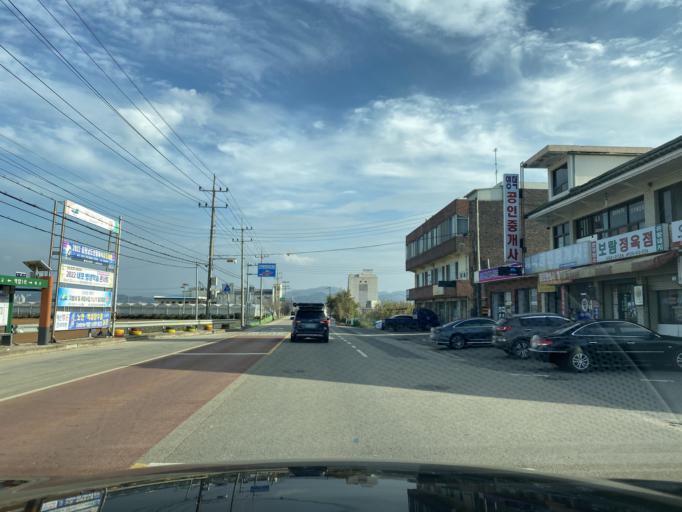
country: KR
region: Chungcheongnam-do
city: Yesan
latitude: 36.6874
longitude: 126.7989
